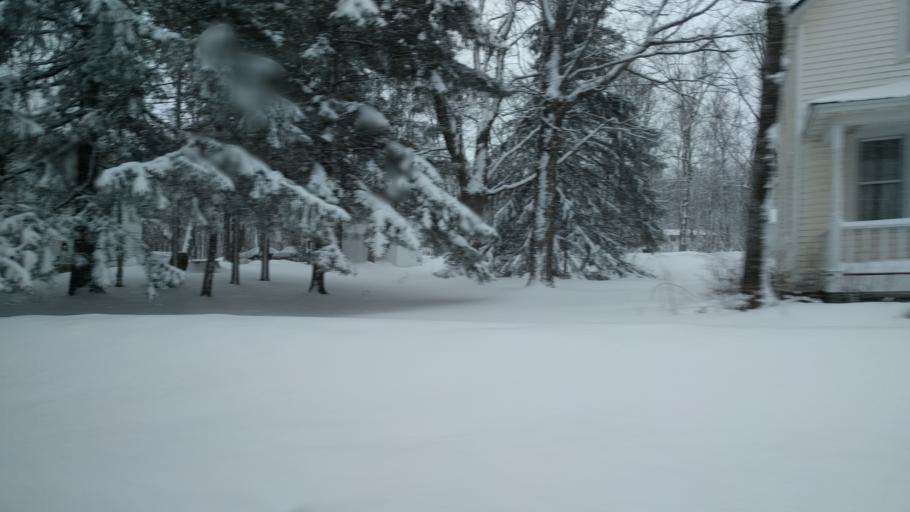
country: US
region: Wisconsin
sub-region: Iron County
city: Hurley
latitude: 46.4285
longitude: -90.2399
